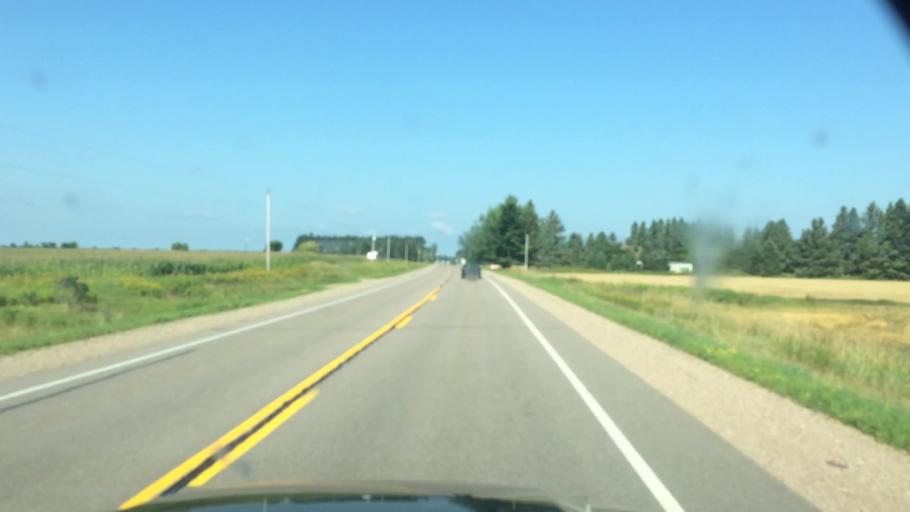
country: US
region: Wisconsin
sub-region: Langlade County
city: Antigo
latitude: 45.1402
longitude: -89.1984
